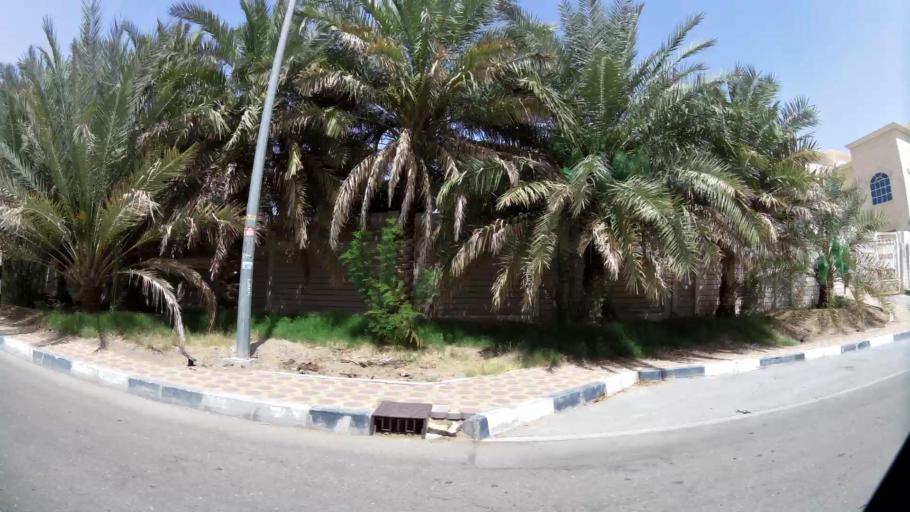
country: AE
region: Abu Dhabi
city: Al Ain
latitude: 24.2579
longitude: 55.6965
